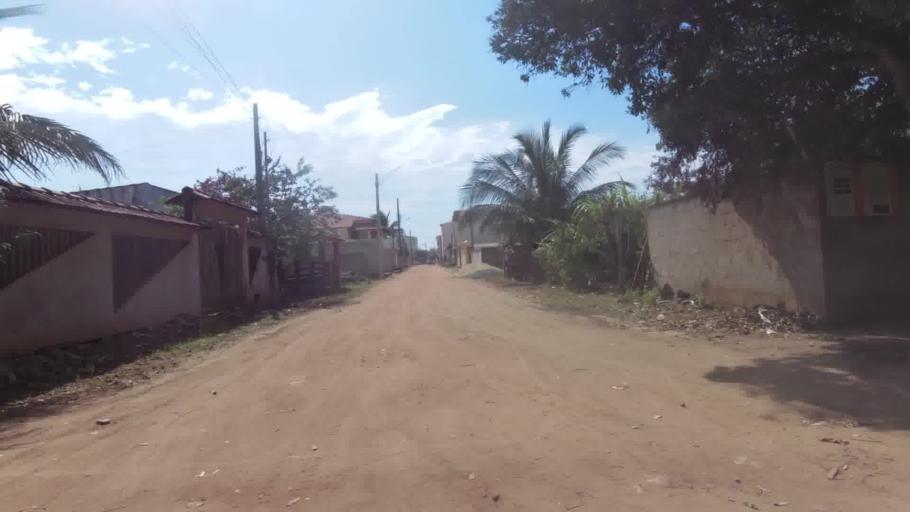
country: BR
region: Espirito Santo
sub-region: Piuma
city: Piuma
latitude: -20.8492
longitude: -40.7488
